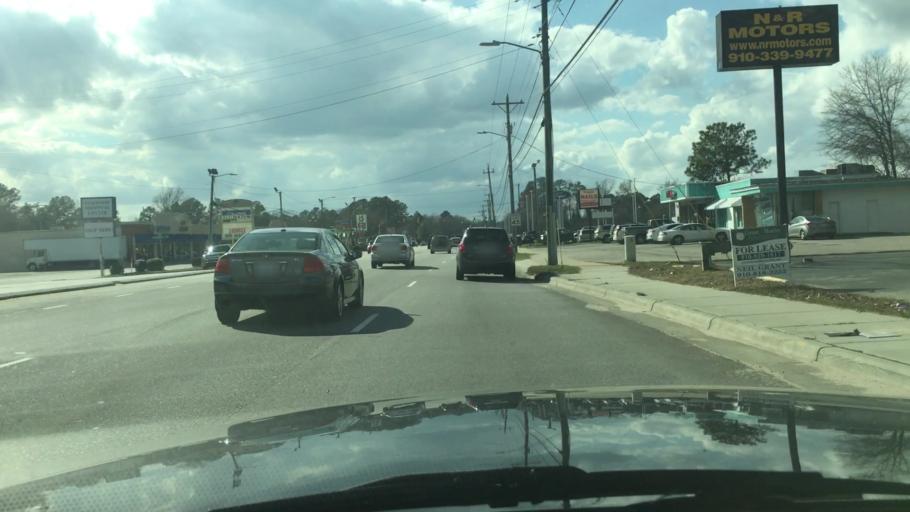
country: US
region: North Carolina
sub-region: Cumberland County
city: Hope Mills
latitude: 35.0429
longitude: -78.9620
